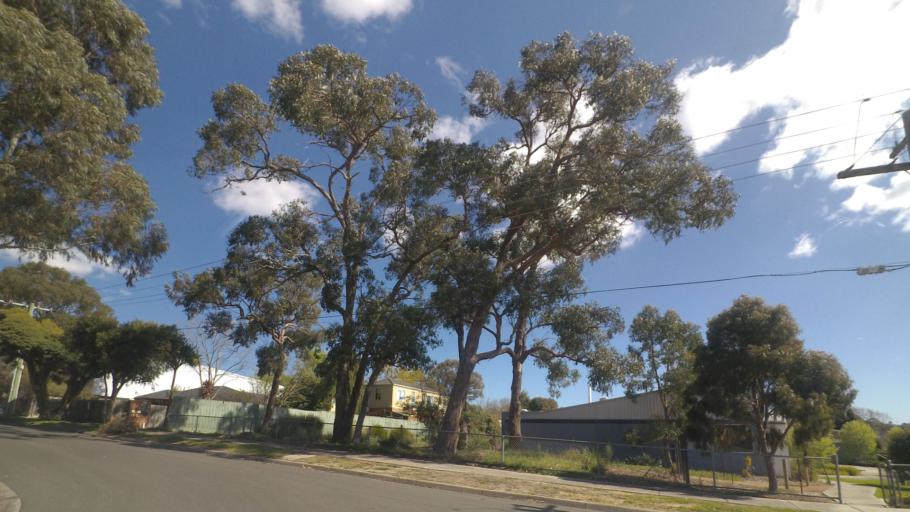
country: AU
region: Victoria
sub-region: Knox
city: Bayswater
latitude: -37.8383
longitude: 145.2634
